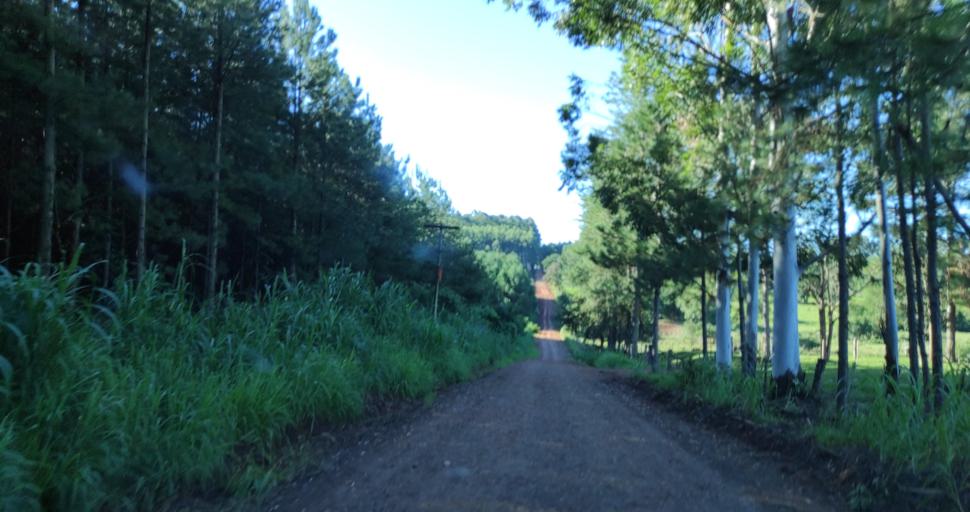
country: AR
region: Misiones
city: Garuhape
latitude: -26.8647
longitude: -55.0049
